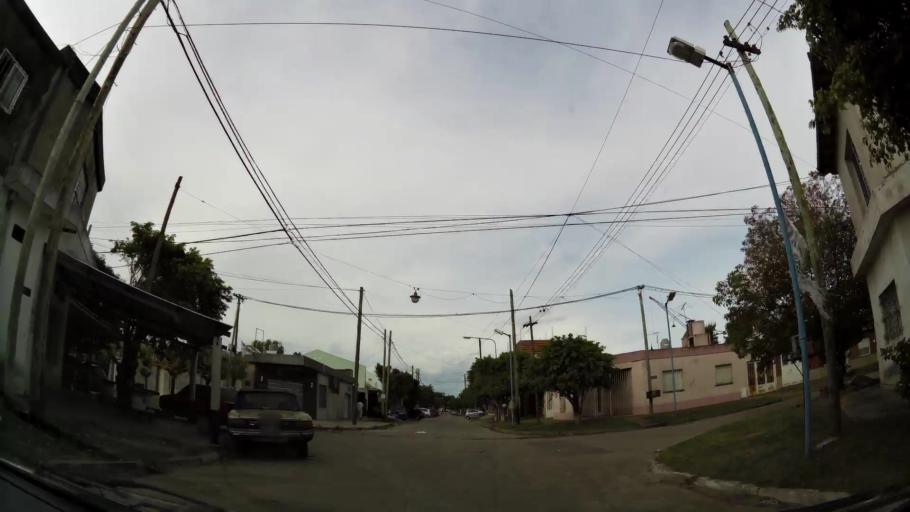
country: AR
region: Buenos Aires
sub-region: Partido de Quilmes
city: Quilmes
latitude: -34.7505
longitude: -58.2819
